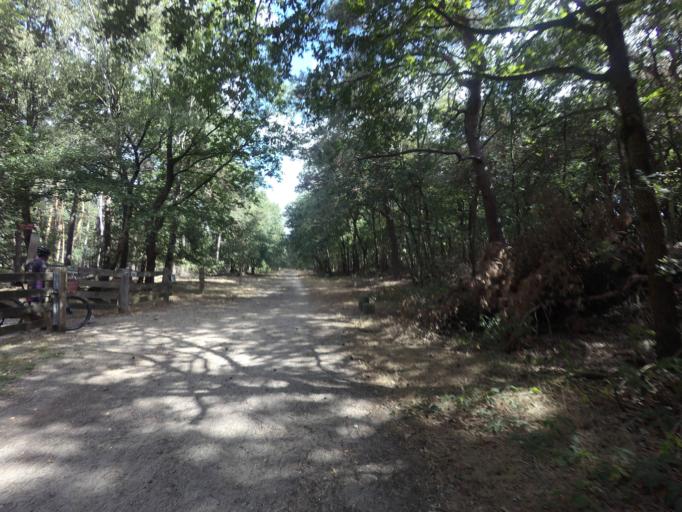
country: NL
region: North Brabant
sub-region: Gemeente Landerd
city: Schaijk
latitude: 51.7536
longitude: 5.6078
